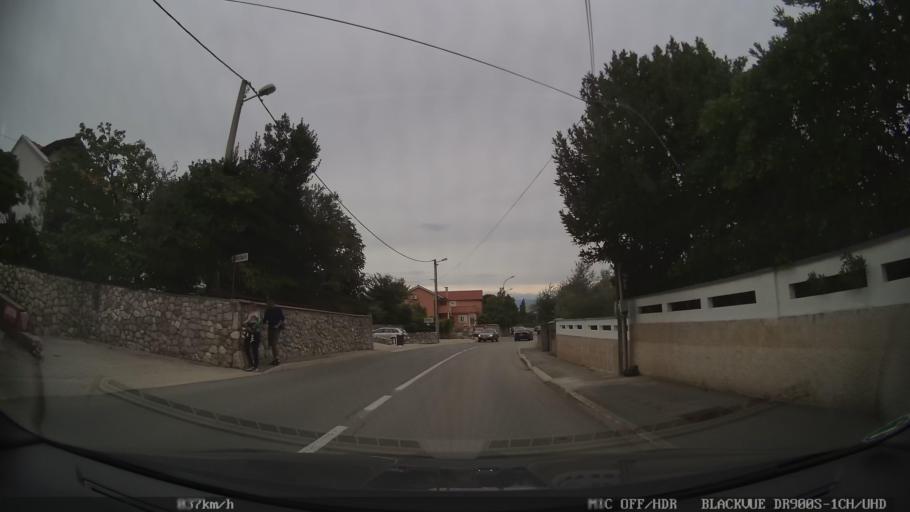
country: HR
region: Primorsko-Goranska
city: Punat
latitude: 44.9758
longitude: 14.7376
